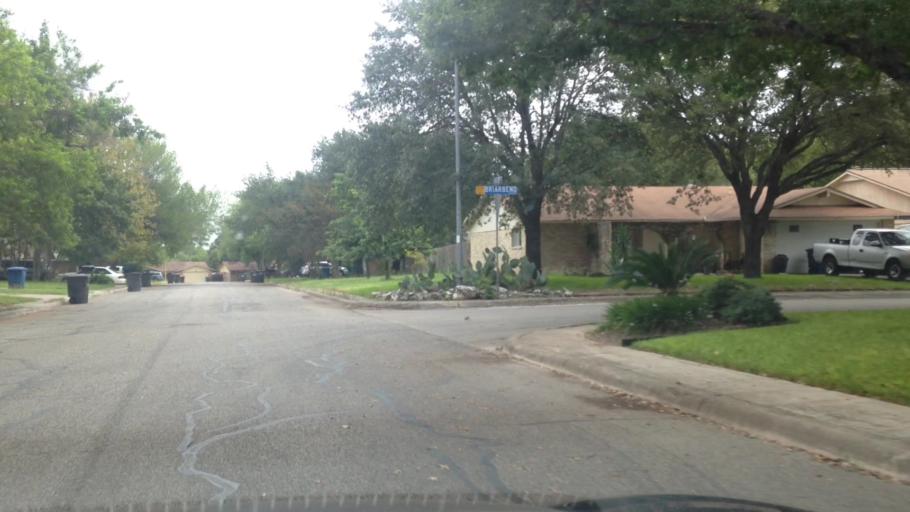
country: US
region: Texas
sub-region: Bexar County
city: Windcrest
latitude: 29.5752
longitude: -98.4135
